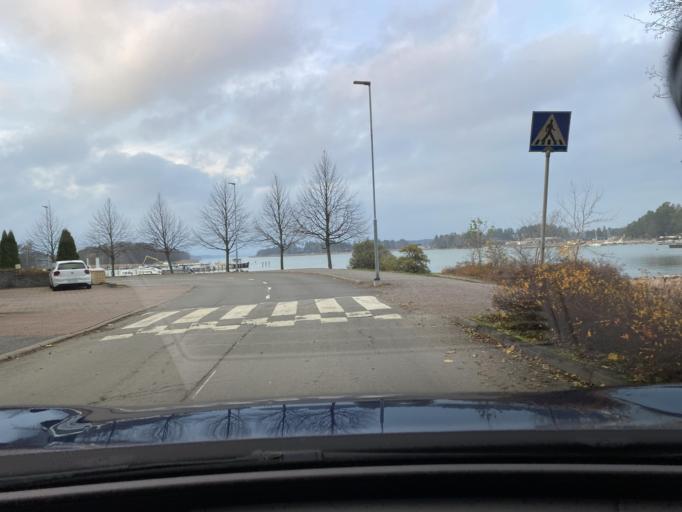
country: FI
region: Varsinais-Suomi
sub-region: Turku
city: Naantali
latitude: 60.4737
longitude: 22.0319
